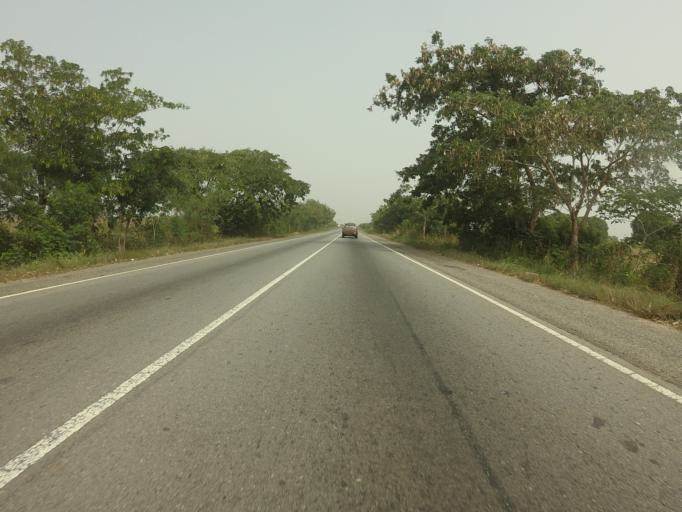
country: GH
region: Volta
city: Anloga
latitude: 5.8888
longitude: 0.4644
